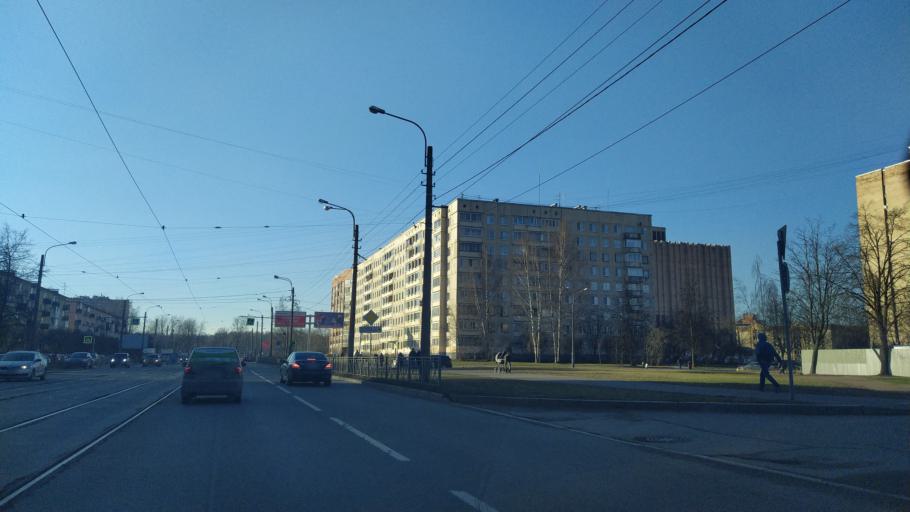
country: RU
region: Leningrad
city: Akademicheskoe
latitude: 60.0165
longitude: 30.3794
